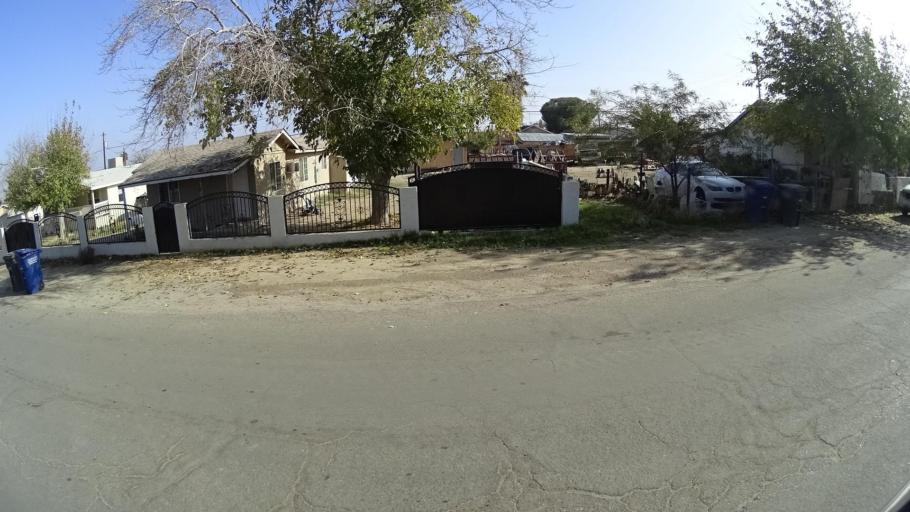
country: US
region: California
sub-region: Kern County
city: South Taft
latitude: 35.1337
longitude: -119.4622
